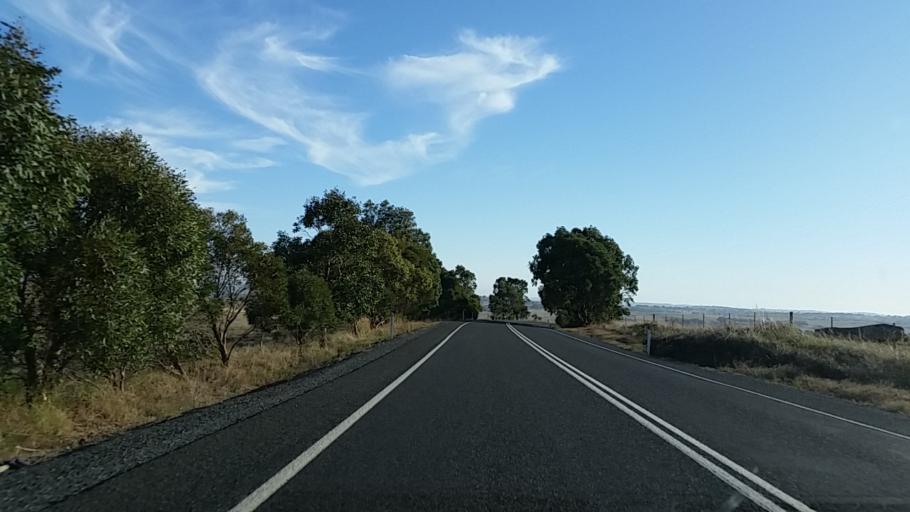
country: AU
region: South Australia
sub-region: Adelaide Hills
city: Birdwood
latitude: -34.7720
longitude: 139.1094
